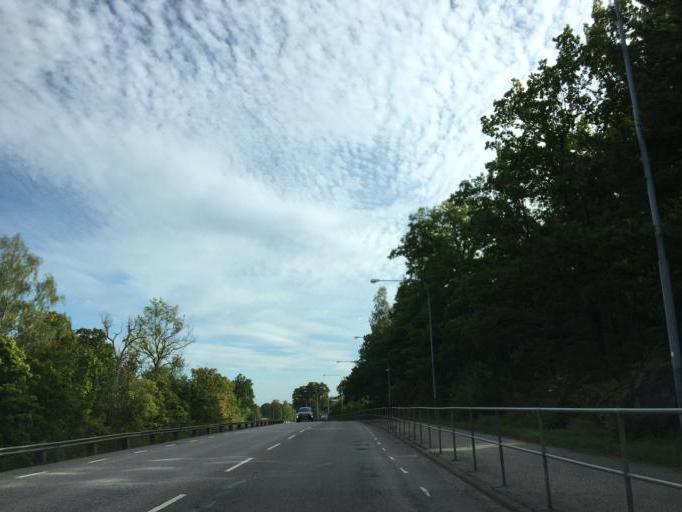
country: SE
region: Soedermanland
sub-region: Eskilstuna Kommun
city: Torshalla
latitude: 59.4212
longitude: 16.4606
